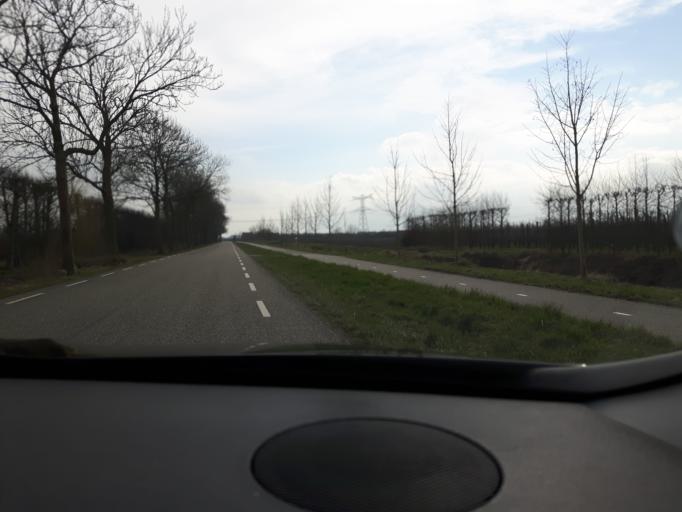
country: NL
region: Zeeland
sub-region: Gemeente Goes
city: Goes
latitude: 51.4426
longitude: 3.9006
